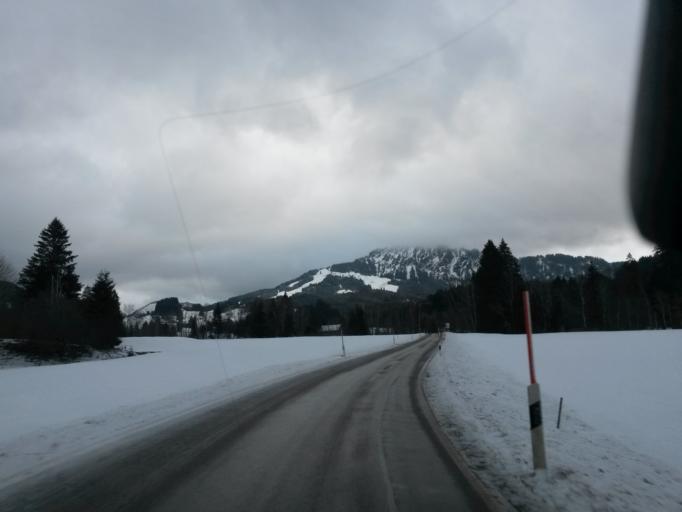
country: DE
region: Bavaria
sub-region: Swabia
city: Wertach
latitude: 47.5809
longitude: 10.4221
